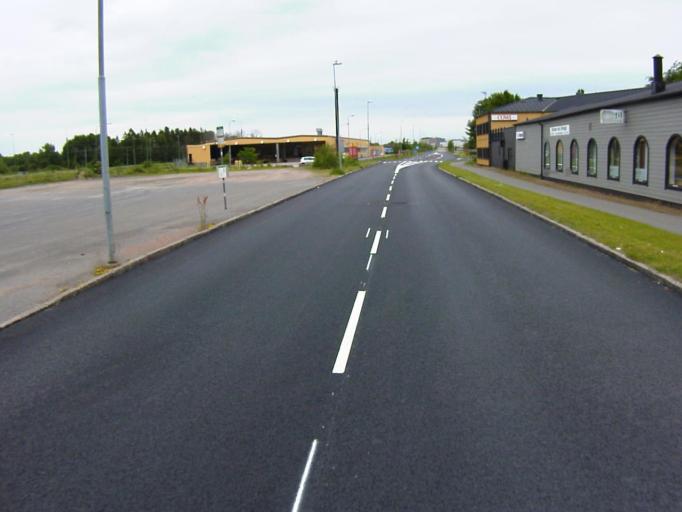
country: SE
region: Skane
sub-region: Kristianstads Kommun
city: Kristianstad
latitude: 56.0373
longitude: 14.1521
